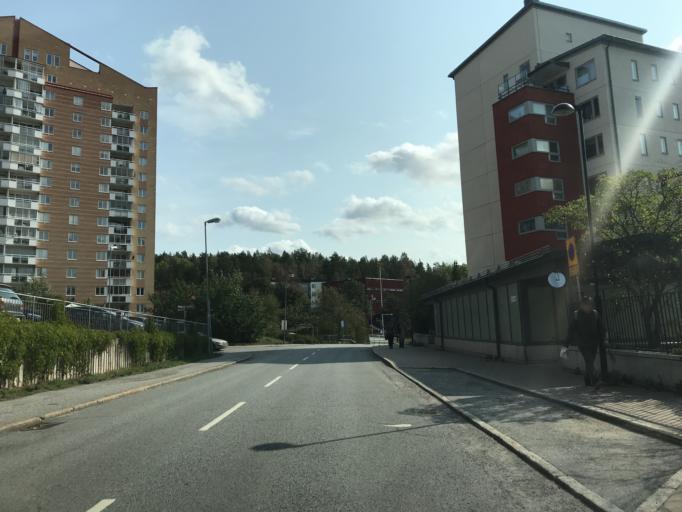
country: SE
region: Stockholm
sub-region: Sollentuna Kommun
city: Sollentuna
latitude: 59.4459
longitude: 17.9666
